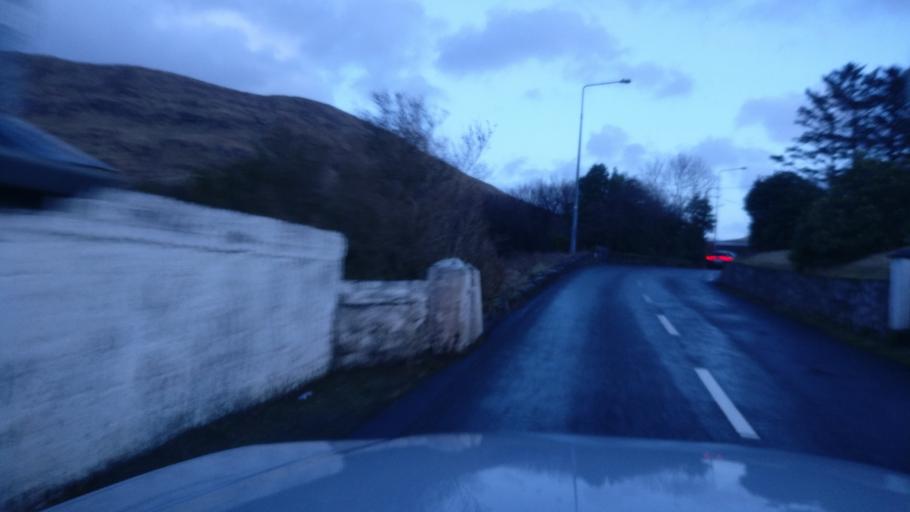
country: IE
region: Connaught
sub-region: Maigh Eo
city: Westport
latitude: 53.5954
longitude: -9.6928
